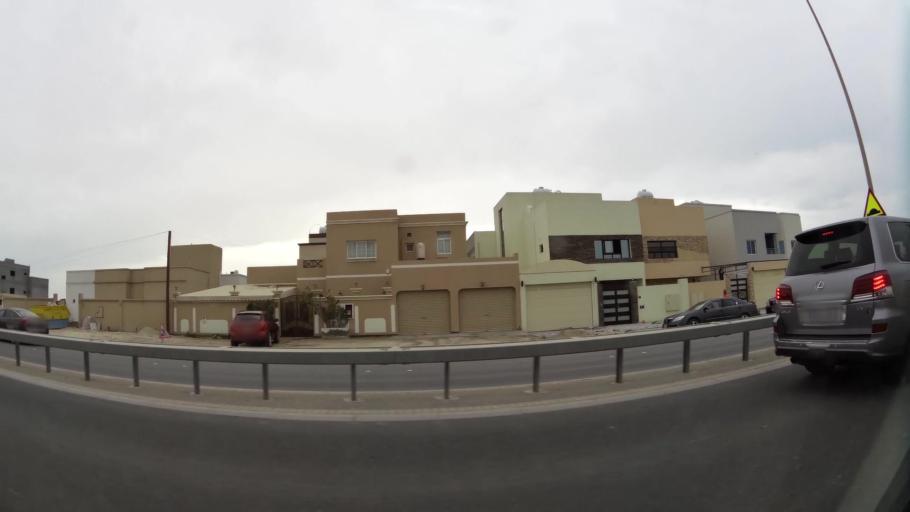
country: BH
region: Central Governorate
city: Madinat Hamad
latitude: 26.0962
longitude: 50.4978
